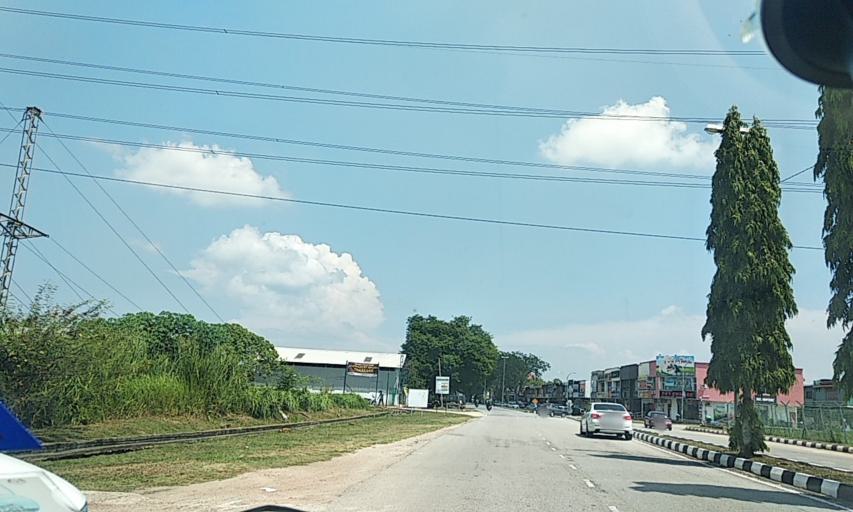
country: MY
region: Kedah
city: Sungai Petani
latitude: 5.6355
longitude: 100.4761
